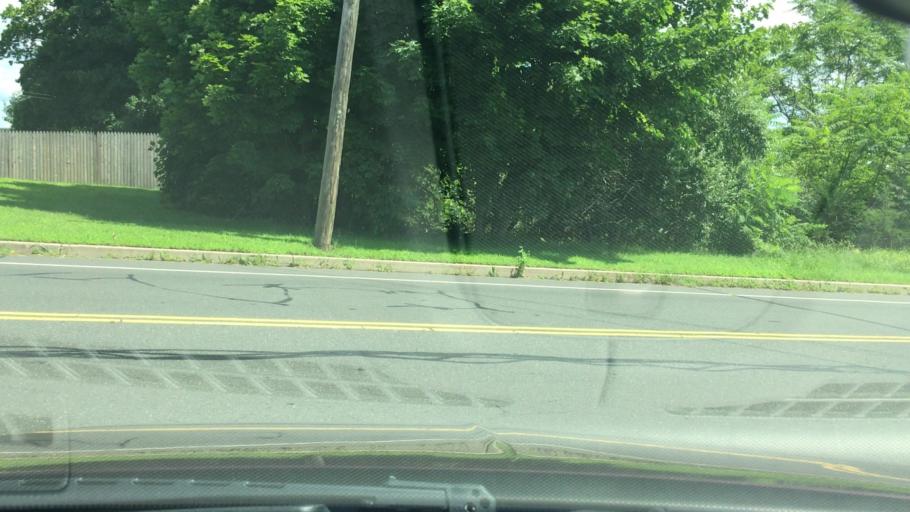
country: US
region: Connecticut
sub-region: Hartford County
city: Kensington
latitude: 41.6421
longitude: -72.7361
